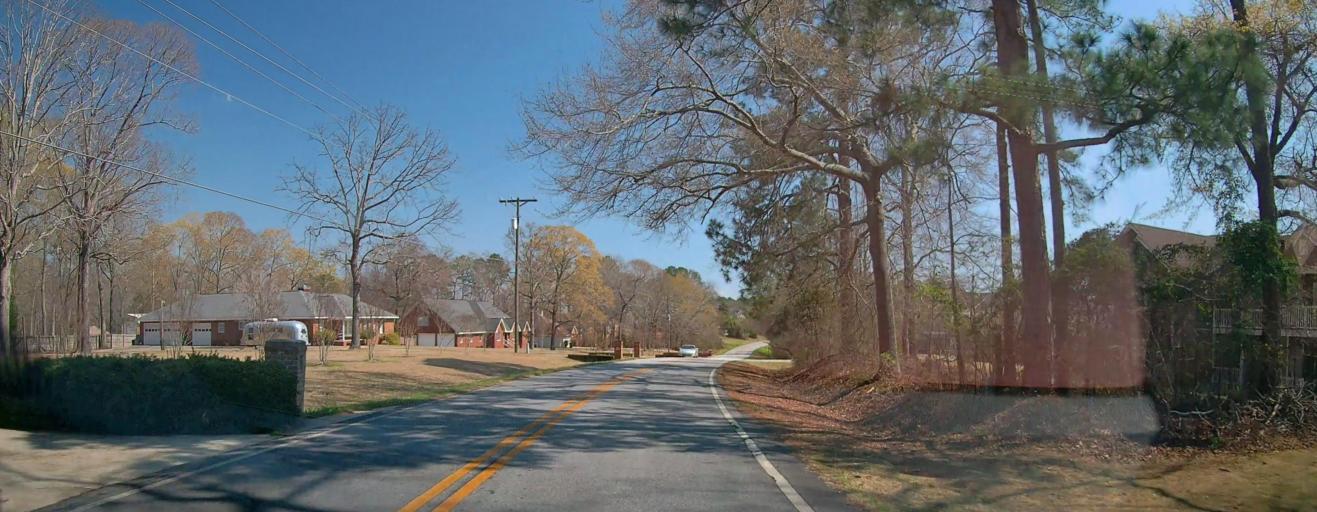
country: US
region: Georgia
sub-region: Houston County
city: Centerville
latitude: 32.5957
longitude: -83.7142
